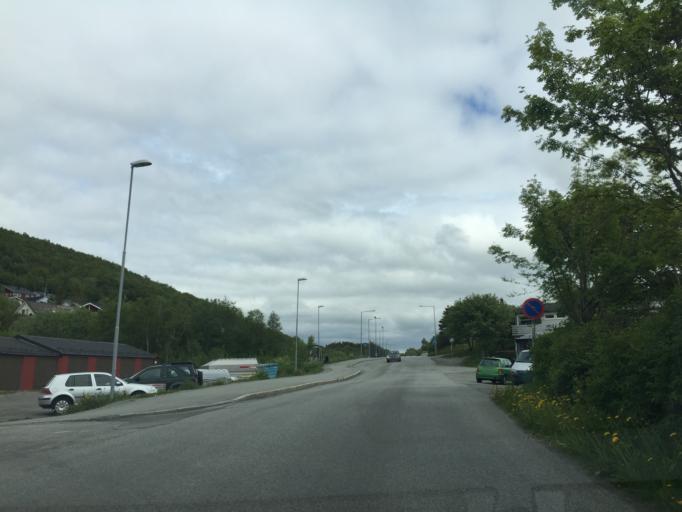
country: NO
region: Nordland
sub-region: Bodo
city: Lopsmarka
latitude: 67.2830
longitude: 14.5280
